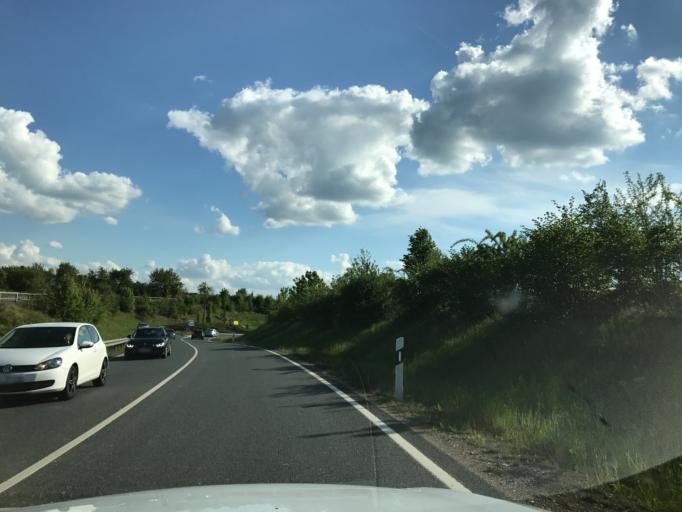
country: DE
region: Bavaria
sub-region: Upper Franconia
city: Igensdorf
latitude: 49.5815
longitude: 11.2061
